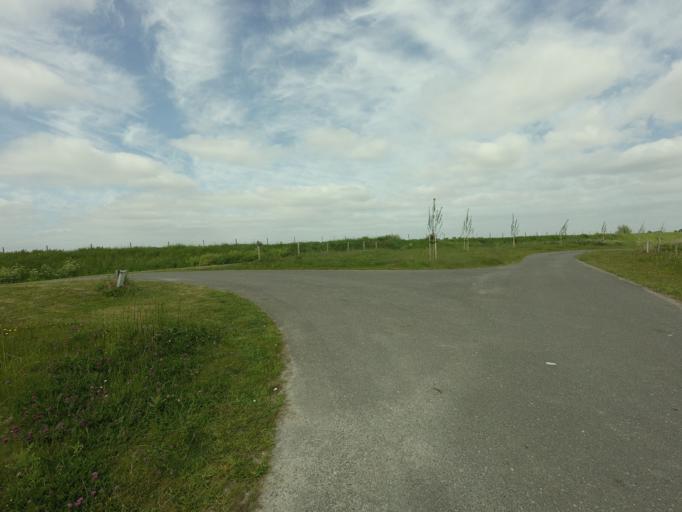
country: NL
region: South Holland
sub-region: Gemeente Spijkenisse
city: Spijkenisse
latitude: 51.7388
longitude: 4.3384
